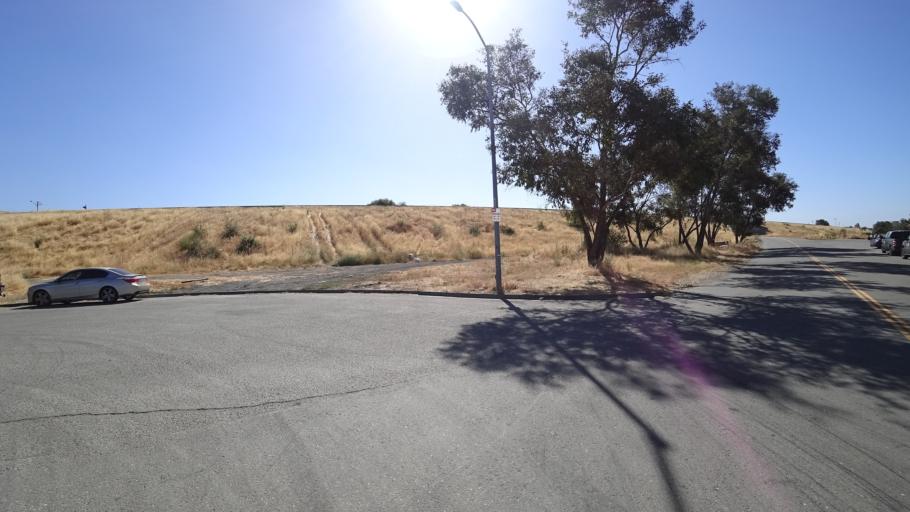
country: US
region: California
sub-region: Alameda County
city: Union City
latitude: 37.6210
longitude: -122.0502
